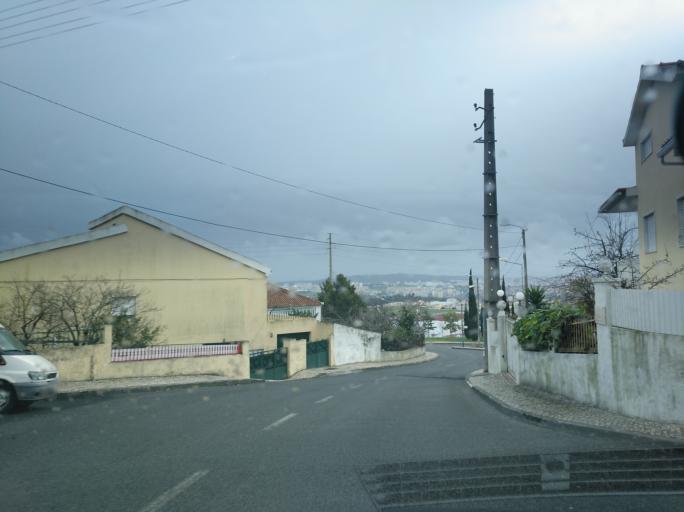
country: PT
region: Lisbon
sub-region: Odivelas
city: Famoes
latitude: 38.7941
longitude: -9.2159
